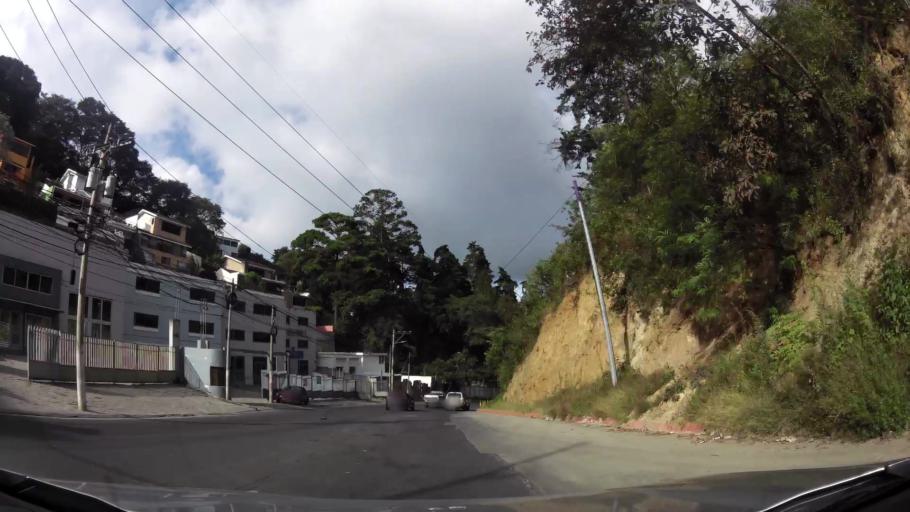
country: GT
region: Guatemala
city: Santa Catarina Pinula
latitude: 14.5670
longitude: -90.4825
